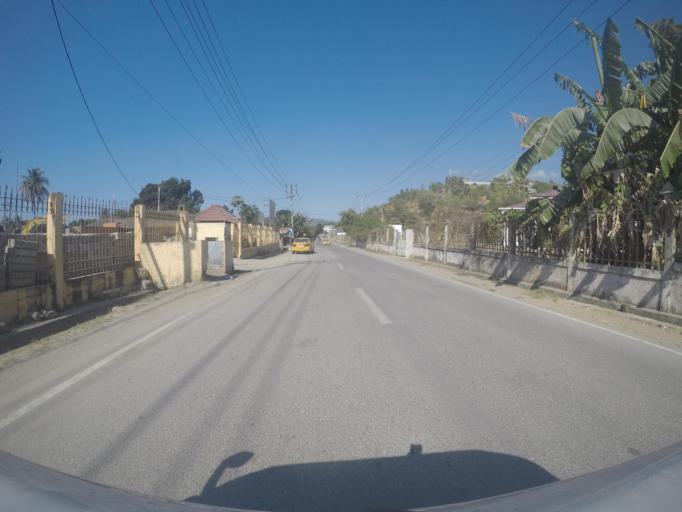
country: TL
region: Dili
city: Dili
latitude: -8.5653
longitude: 125.5554
